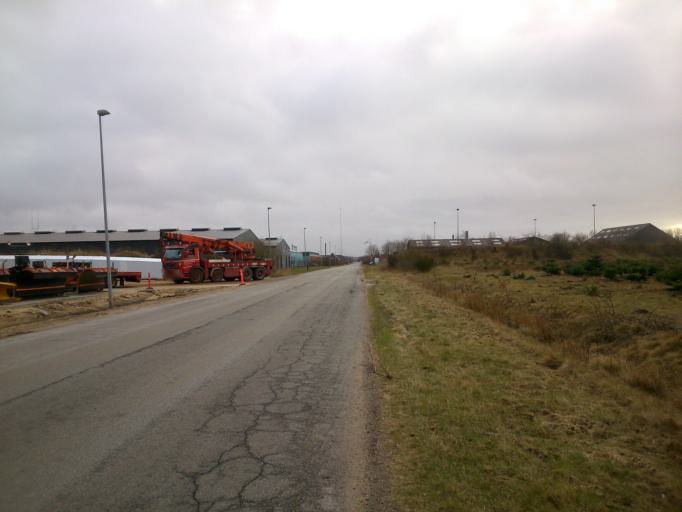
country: DK
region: Central Jutland
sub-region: Ringkobing-Skjern Kommune
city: Skjern
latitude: 55.9645
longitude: 8.4968
